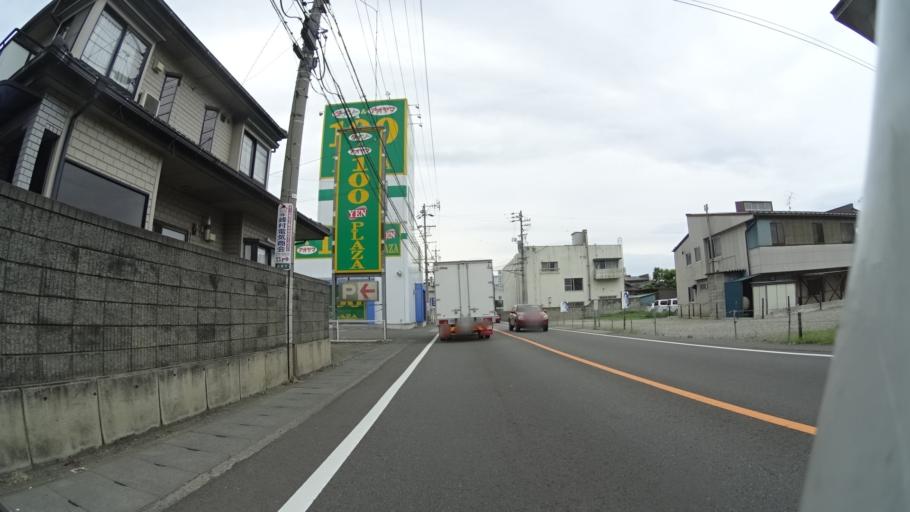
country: JP
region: Nagano
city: Nagano-shi
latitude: 36.5307
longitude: 138.1233
